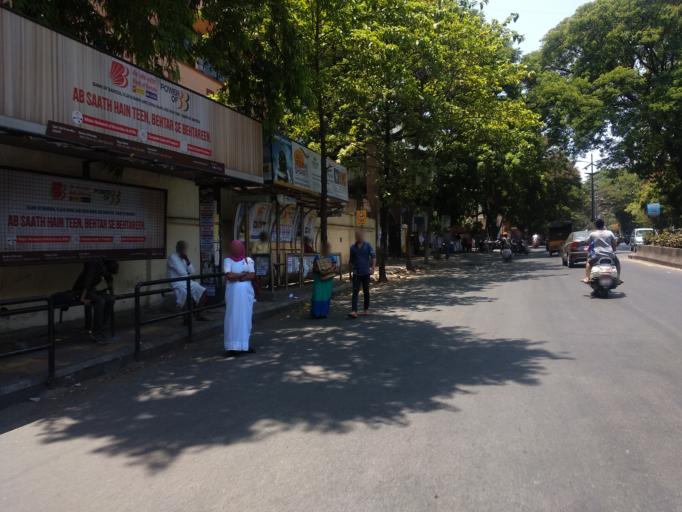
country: IN
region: Maharashtra
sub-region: Pune Division
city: Pune
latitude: 18.5087
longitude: 73.8440
